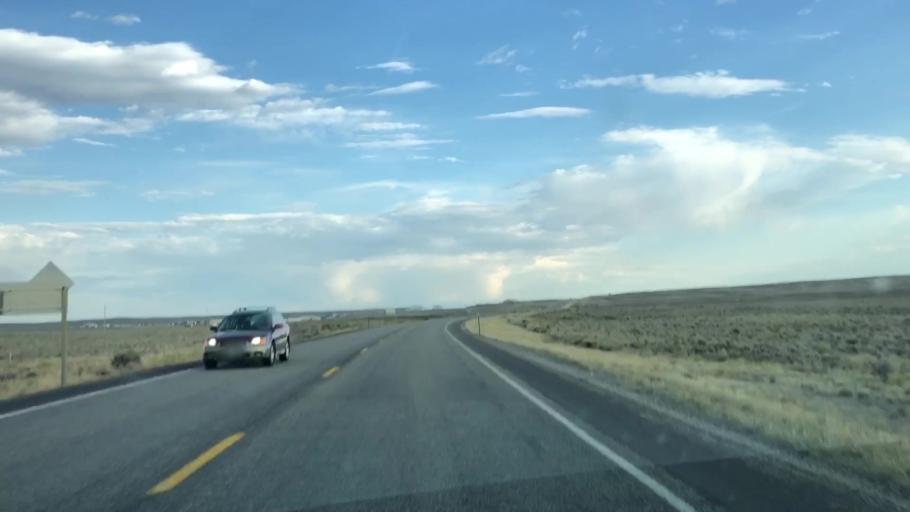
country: US
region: Wyoming
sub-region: Sublette County
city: Pinedale
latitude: 42.6185
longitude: -109.6500
